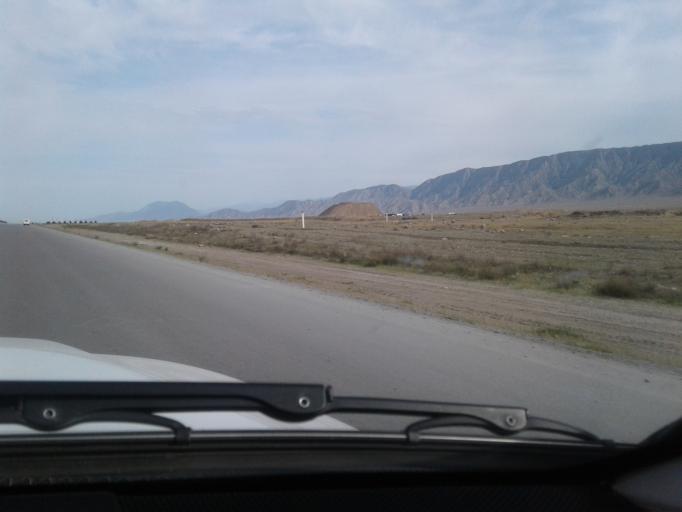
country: TM
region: Ahal
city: Baharly
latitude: 38.2243
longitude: 57.7961
